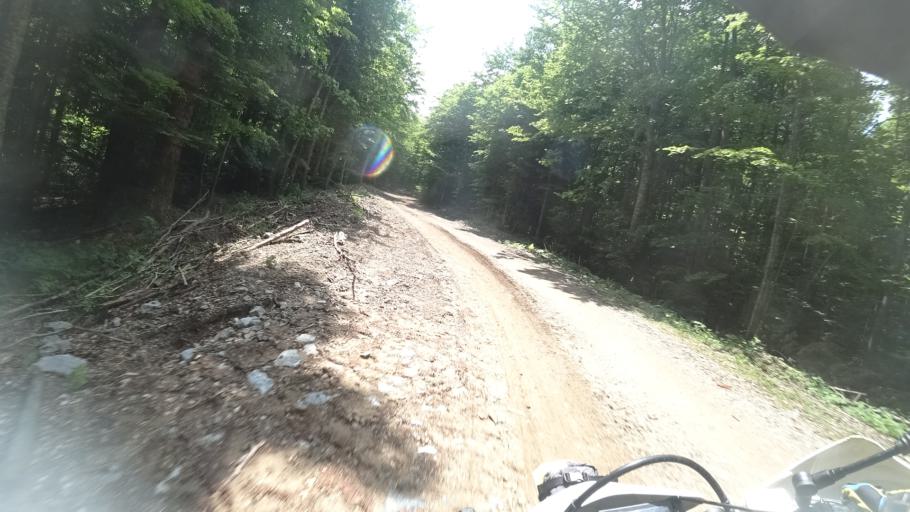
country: HR
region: Zadarska
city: Gracac
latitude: 44.4899
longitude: 15.8729
